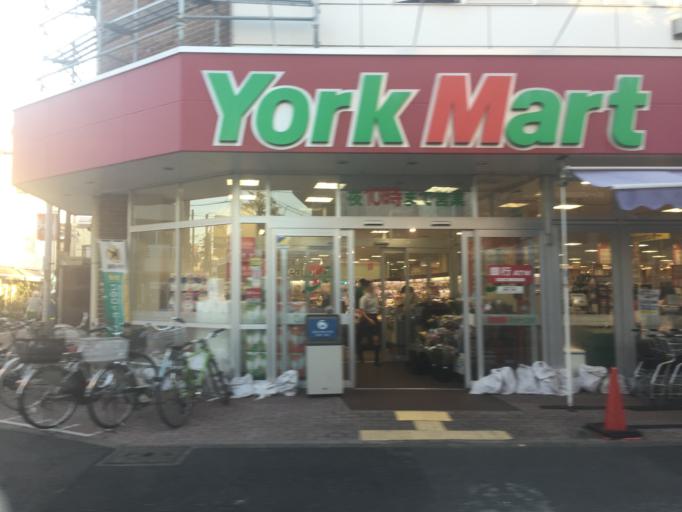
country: JP
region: Tokyo
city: Tokyo
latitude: 35.6199
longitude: 139.6415
